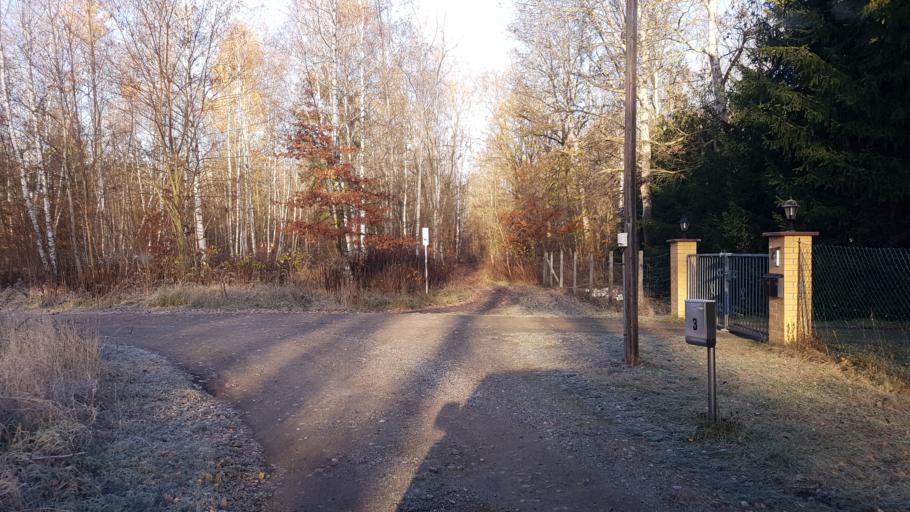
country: DE
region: Brandenburg
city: Sallgast
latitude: 51.5661
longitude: 13.8719
